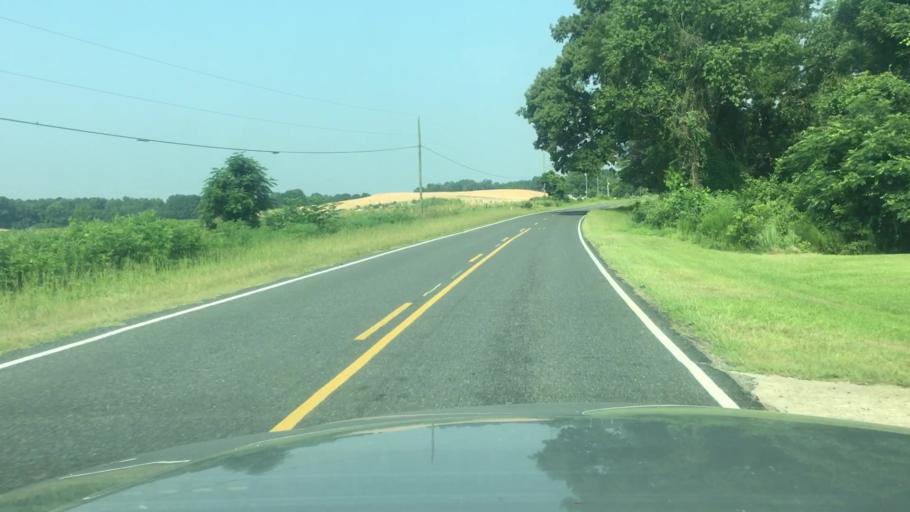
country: US
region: North Carolina
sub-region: Cumberland County
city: Hope Mills
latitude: 34.9092
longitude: -78.8614
